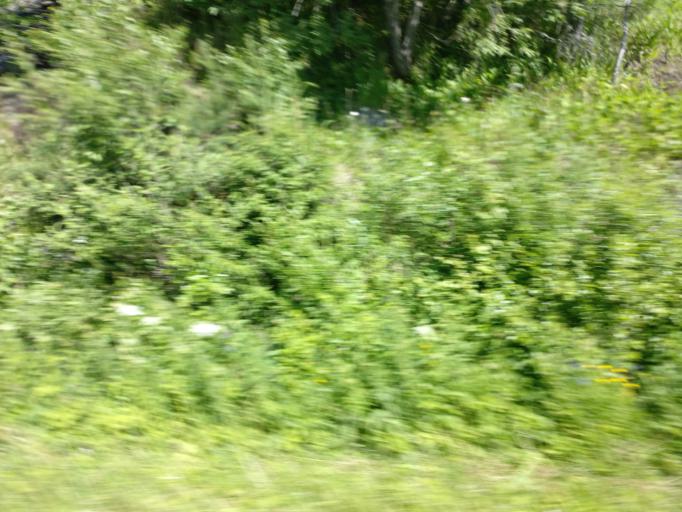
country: FI
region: Southern Savonia
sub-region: Savonlinna
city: Rantasalmi
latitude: 62.1343
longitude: 28.2442
